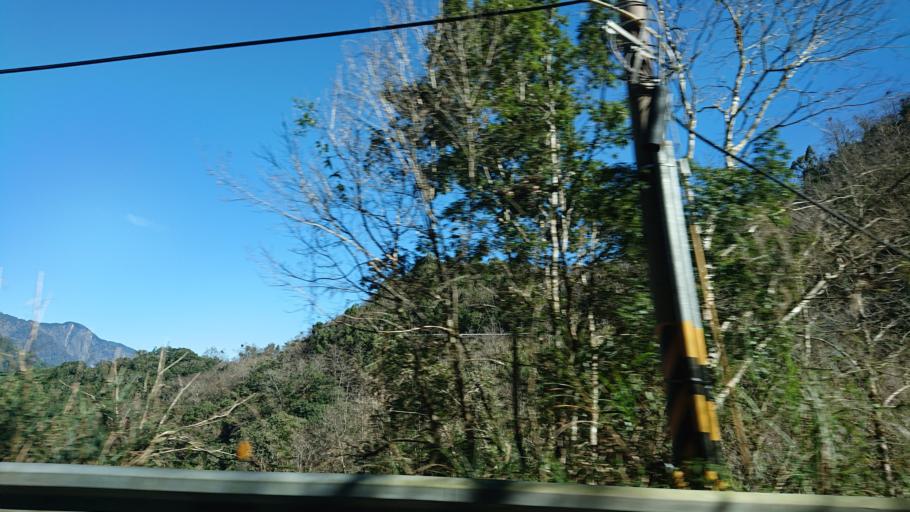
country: TW
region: Taiwan
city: Daxi
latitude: 24.4028
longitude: 121.3661
